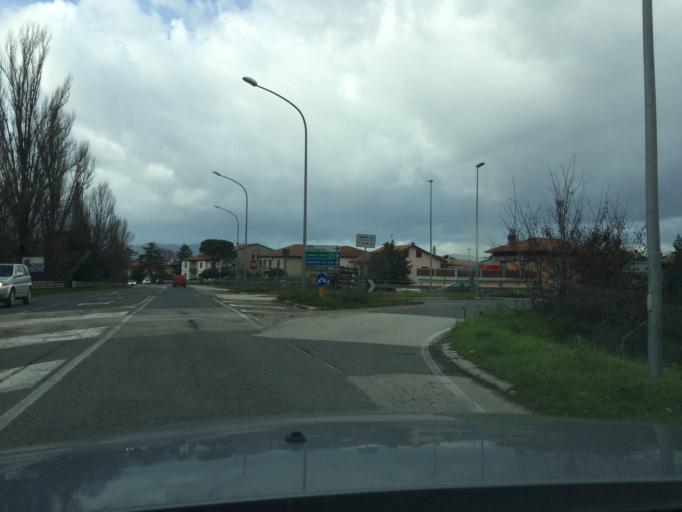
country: IT
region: Umbria
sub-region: Provincia di Terni
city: Terni
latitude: 42.5456
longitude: 12.6020
